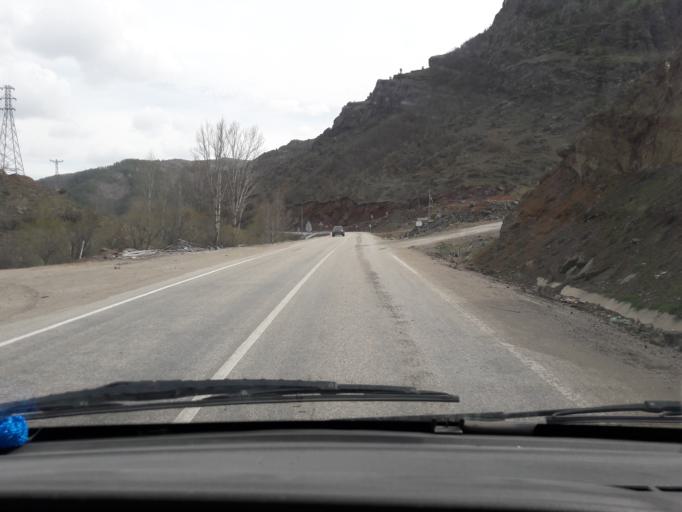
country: TR
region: Gumushane
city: Gumushkhane
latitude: 40.2988
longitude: 39.4734
